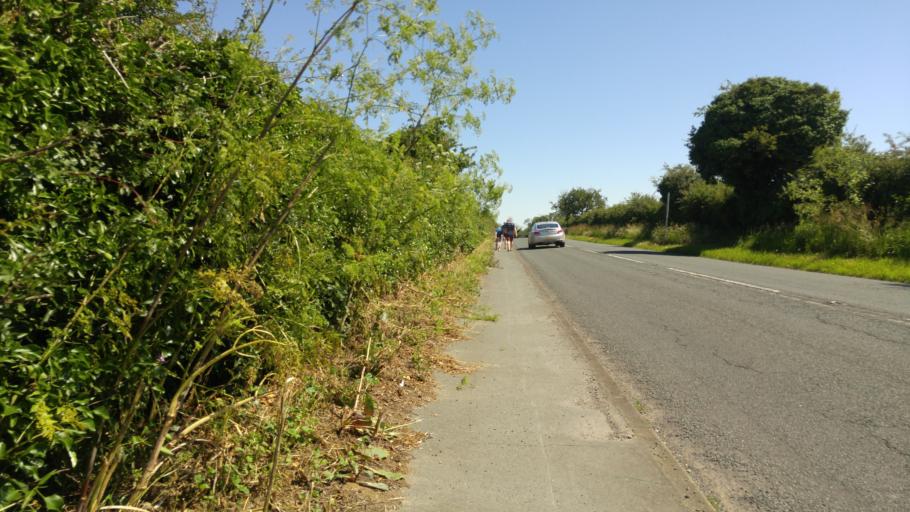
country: GB
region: England
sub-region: Essex
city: Rowhedge
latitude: 51.8622
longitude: 0.9376
